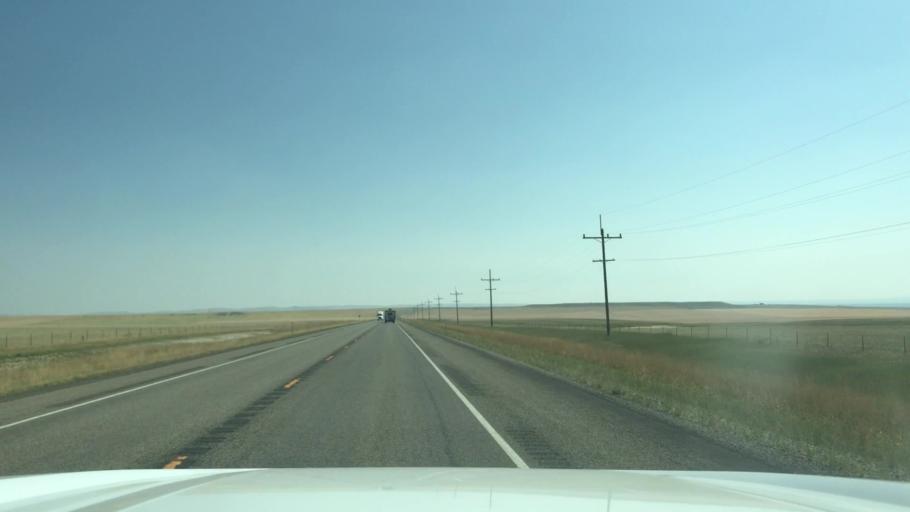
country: US
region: Montana
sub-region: Wheatland County
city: Harlowton
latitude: 46.4997
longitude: -109.7661
